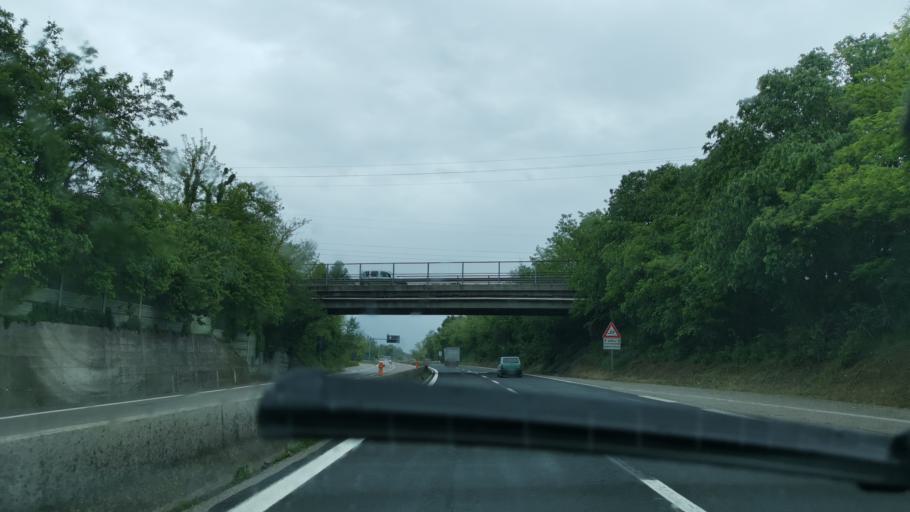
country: IT
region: Veneto
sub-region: Provincia di Verona
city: Cola
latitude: 45.4657
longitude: 10.7600
